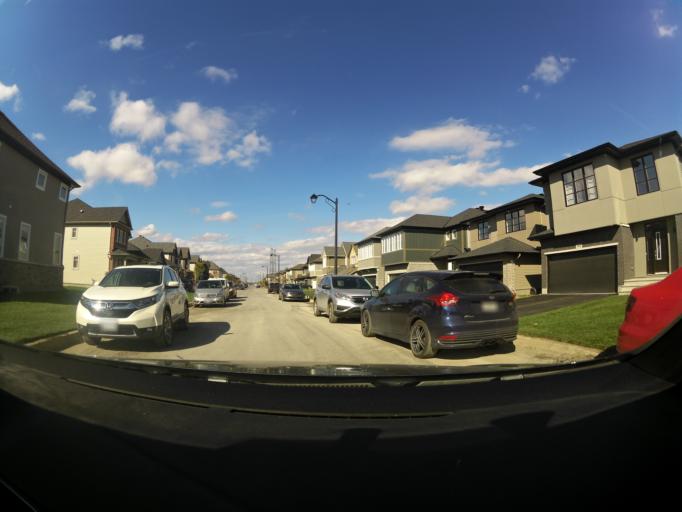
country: CA
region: Ontario
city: Bells Corners
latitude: 45.2769
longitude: -75.8789
